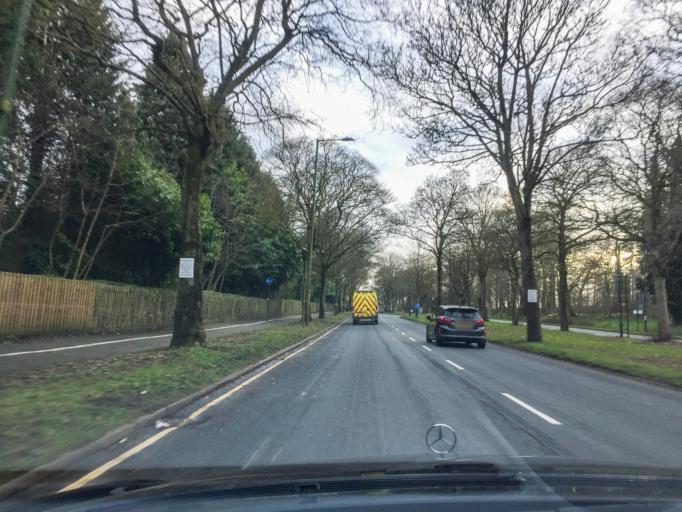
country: GB
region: England
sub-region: City and Borough of Birmingham
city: Bartley Green
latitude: 52.4233
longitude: -1.9581
